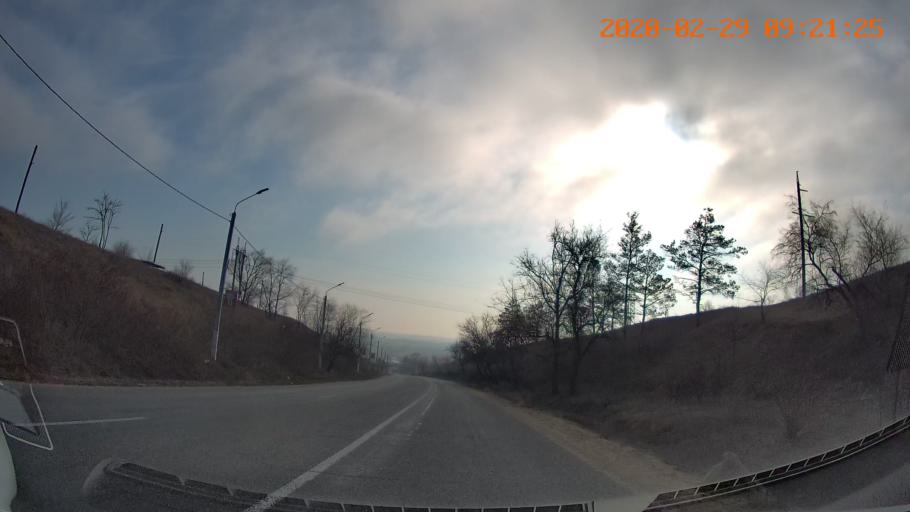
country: MD
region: Telenesti
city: Pervomaisc
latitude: 46.7388
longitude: 29.9581
